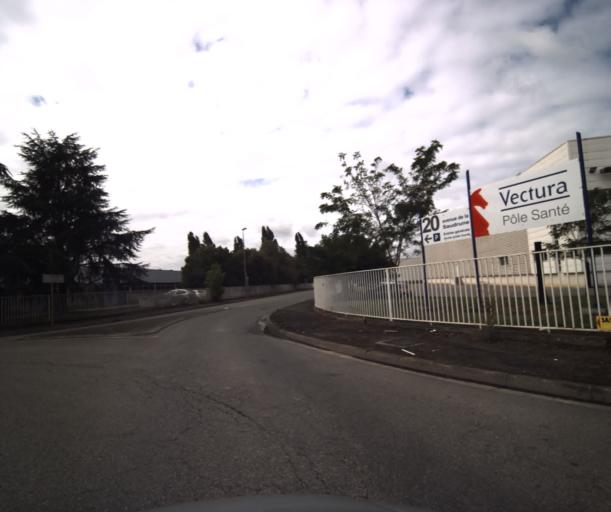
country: FR
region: Midi-Pyrenees
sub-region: Departement de la Haute-Garonne
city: Pinsaguel
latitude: 43.5294
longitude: 1.3798
